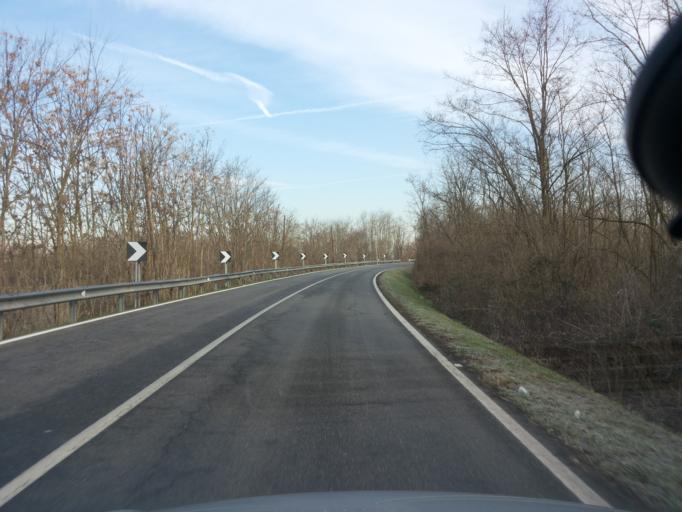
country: IT
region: Piedmont
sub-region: Provincia di Vercelli
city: Quinto Vercellese
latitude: 45.3794
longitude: 8.3724
